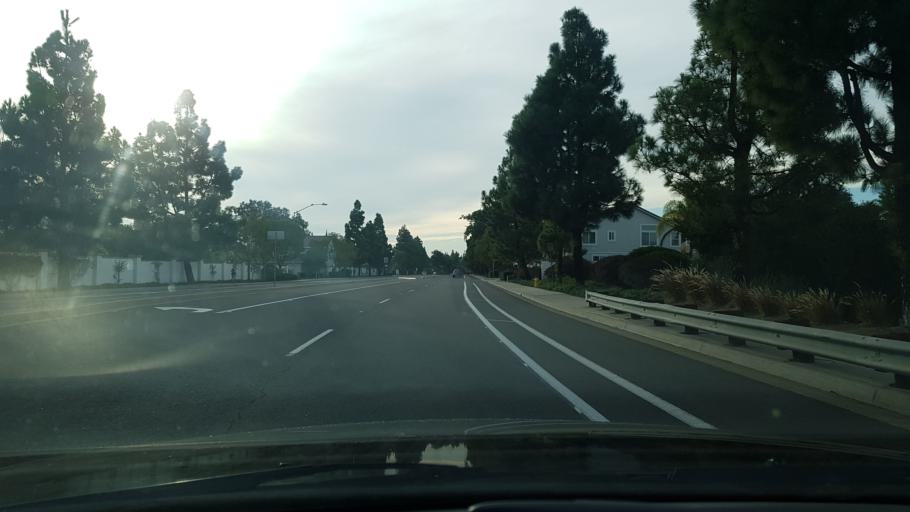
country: US
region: California
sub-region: San Diego County
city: Fairbanks Ranch
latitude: 32.9145
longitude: -117.1931
